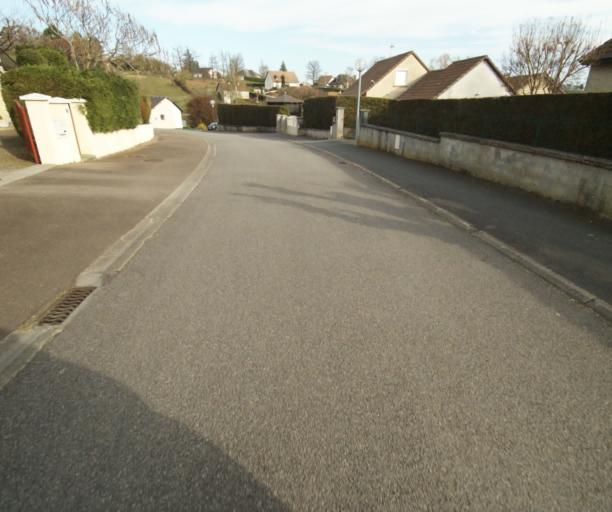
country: FR
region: Limousin
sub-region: Departement de la Correze
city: Naves
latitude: 45.3187
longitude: 1.7572
